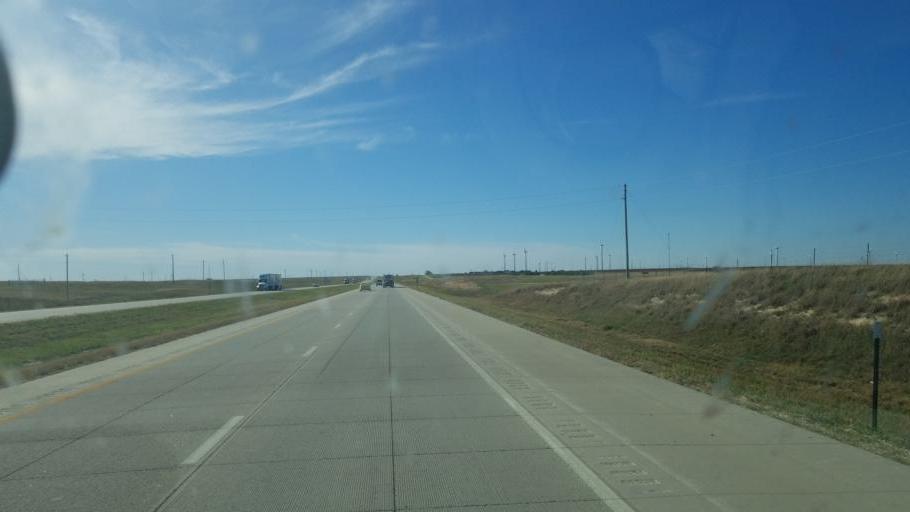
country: US
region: Kansas
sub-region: Ellsworth County
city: Ellsworth
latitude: 38.8486
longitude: -98.1872
